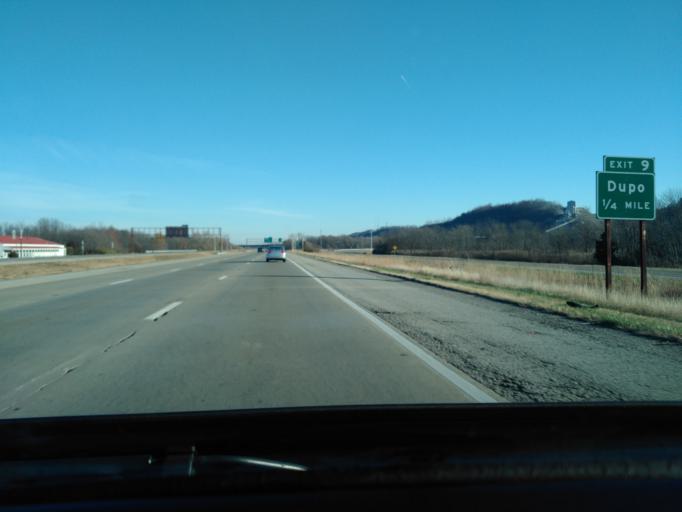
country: US
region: Illinois
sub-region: Saint Clair County
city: Dupo
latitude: 38.5005
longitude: -90.2107
